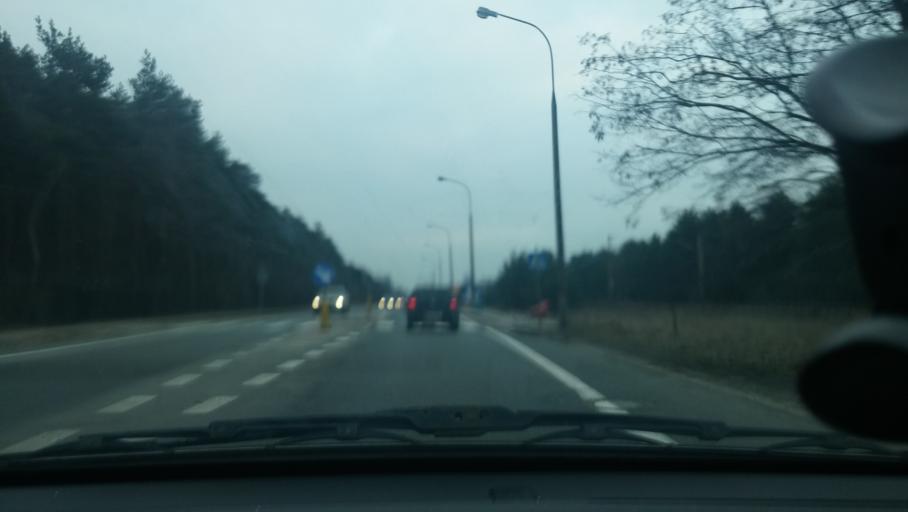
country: PL
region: Masovian Voivodeship
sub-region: Warszawa
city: Wawer
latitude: 52.1982
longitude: 21.1752
